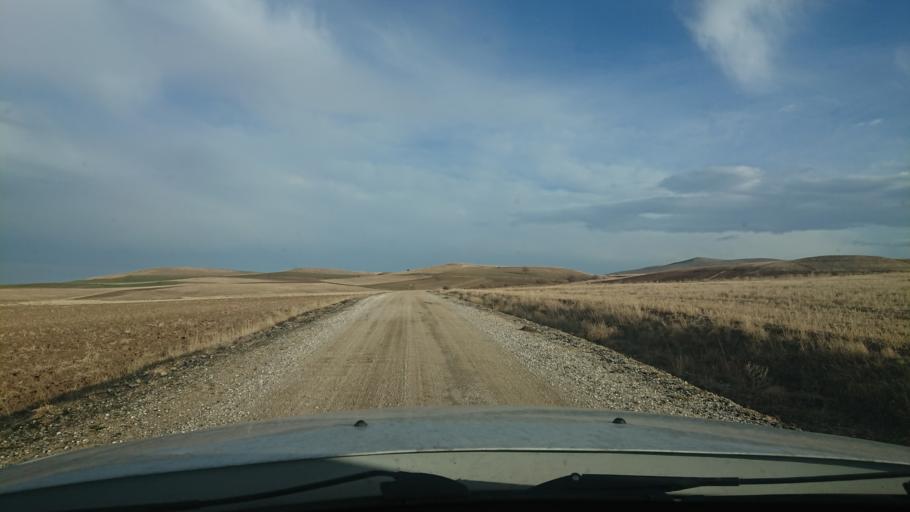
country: TR
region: Aksaray
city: Acipinar
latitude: 38.6912
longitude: 33.8701
